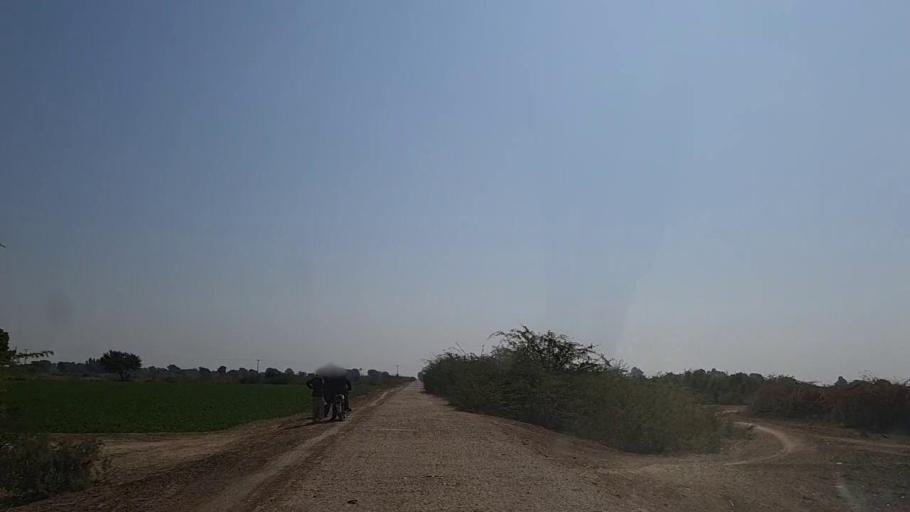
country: PK
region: Sindh
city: Digri
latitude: 24.9793
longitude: 69.2049
